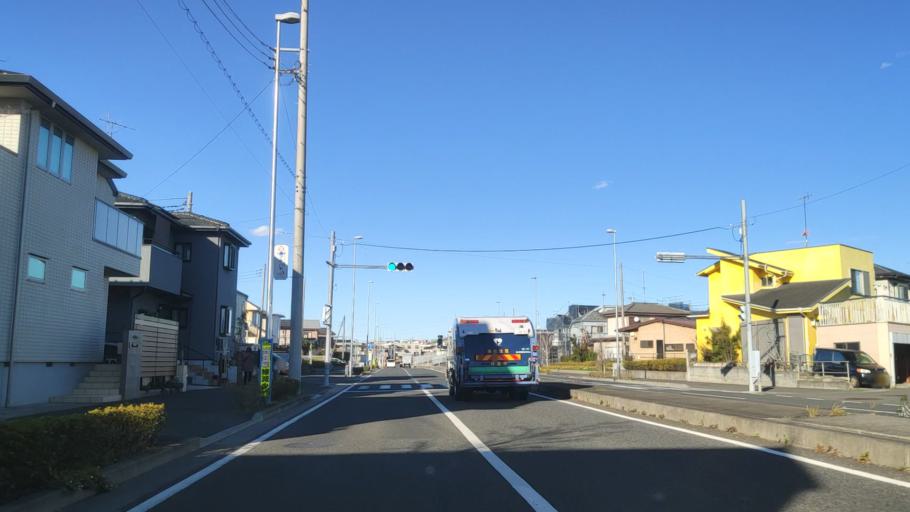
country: JP
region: Tokyo
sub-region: Machida-shi
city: Machida
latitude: 35.5228
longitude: 139.5452
